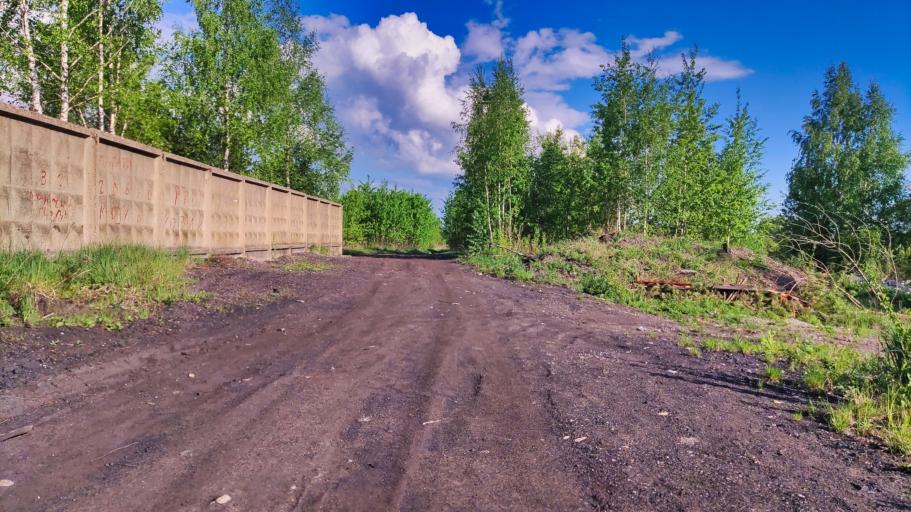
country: RU
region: Tverskaya
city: Rzhev
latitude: 56.2402
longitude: 34.3412
